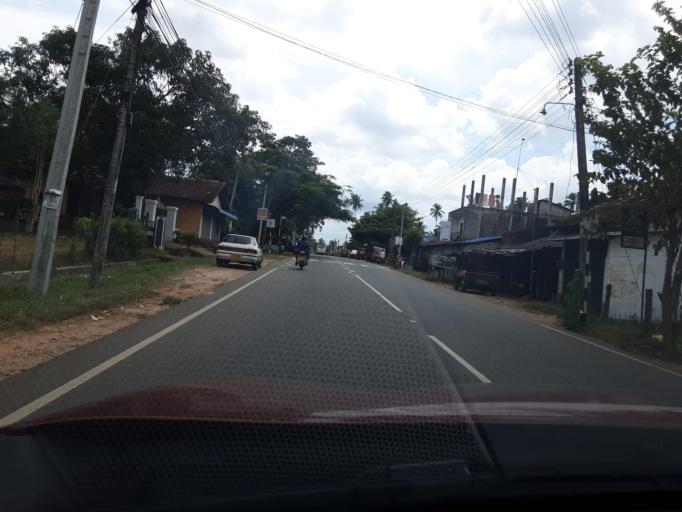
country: LK
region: North Western
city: Kuliyapitiya
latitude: 7.4513
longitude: 80.1697
